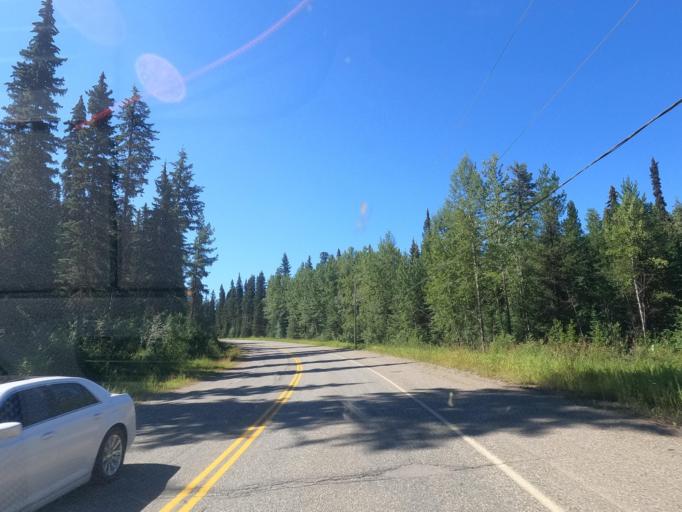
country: CA
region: British Columbia
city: Quesnel
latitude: 53.0399
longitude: -122.2604
